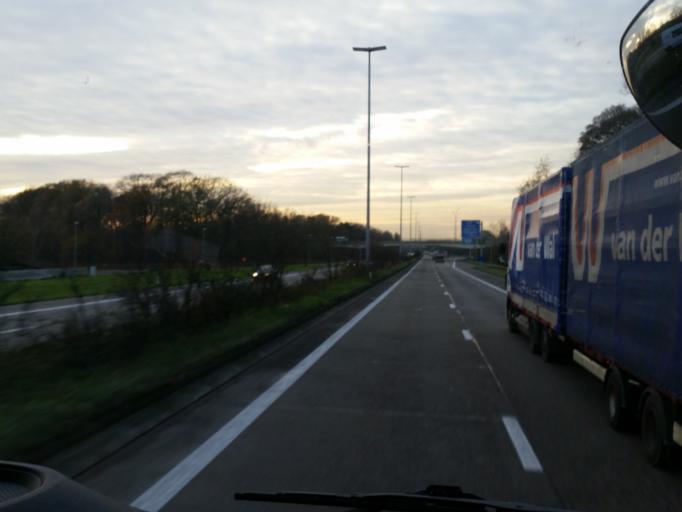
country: BE
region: Flanders
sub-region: Provincie Antwerpen
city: Vosselaar
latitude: 51.2974
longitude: 4.9175
